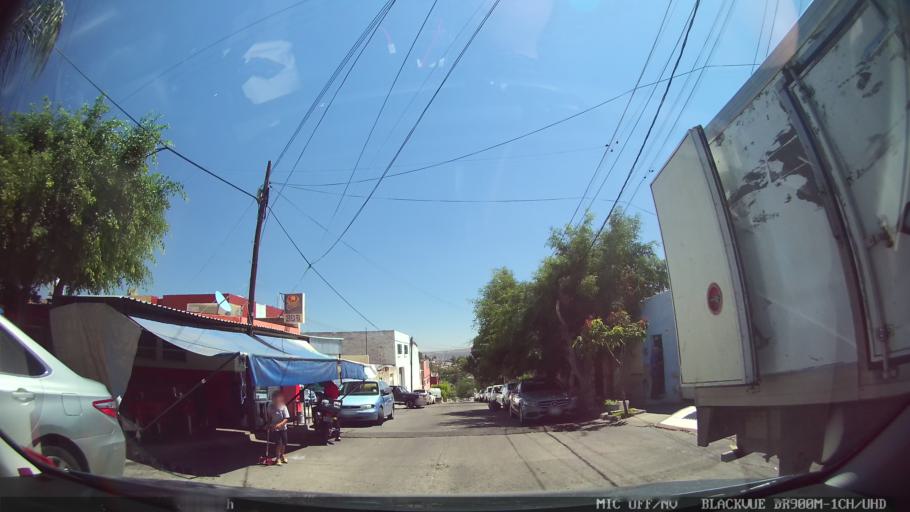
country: MX
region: Jalisco
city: Tlaquepaque
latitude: 20.6909
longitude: -103.2908
